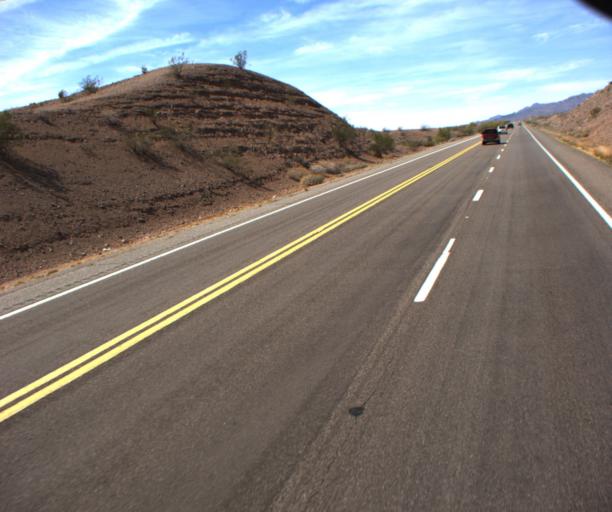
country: US
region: Arizona
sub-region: Mohave County
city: Lake Havasu City
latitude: 34.3773
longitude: -114.1640
